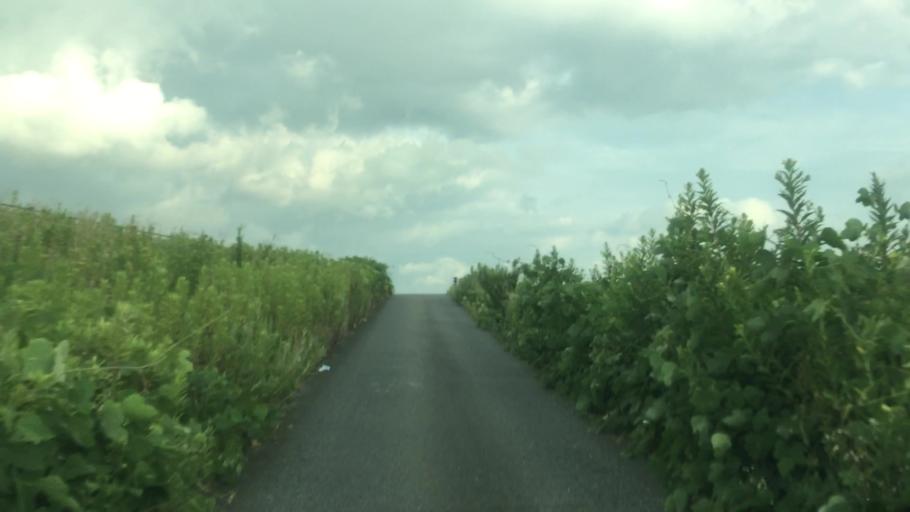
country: JP
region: Hyogo
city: Toyooka
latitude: 35.5643
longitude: 134.8118
